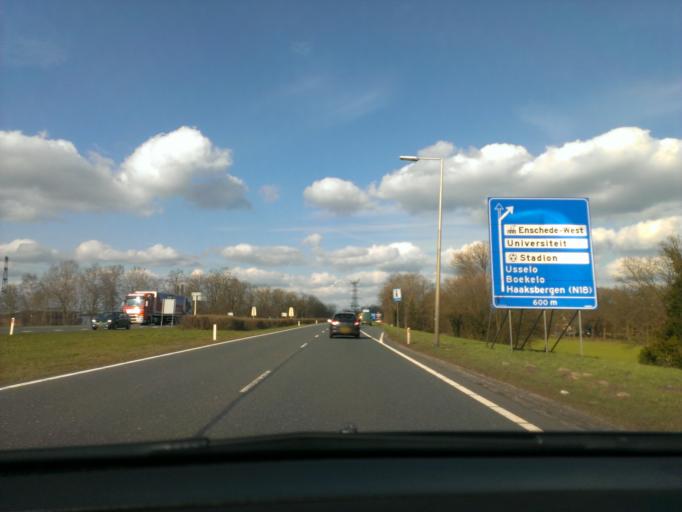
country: NL
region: Overijssel
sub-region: Gemeente Hengelo
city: Hengelo
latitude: 52.2086
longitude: 6.8252
